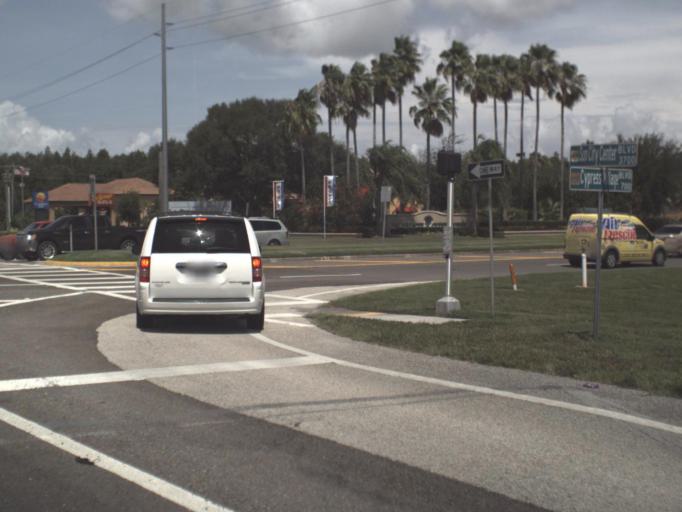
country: US
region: Florida
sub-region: Hillsborough County
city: Sun City Center
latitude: 27.7125
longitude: -82.3767
